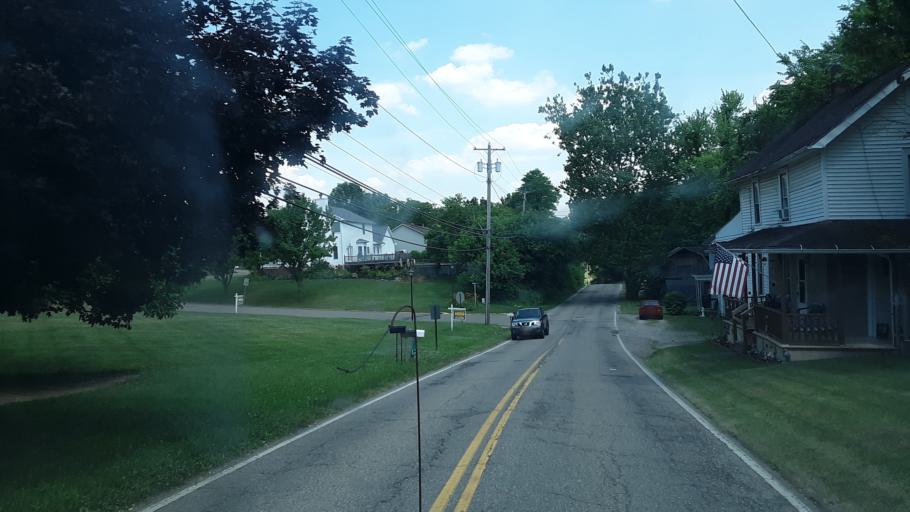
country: US
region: Ohio
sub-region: Stark County
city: Navarre
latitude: 40.7220
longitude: -81.5155
